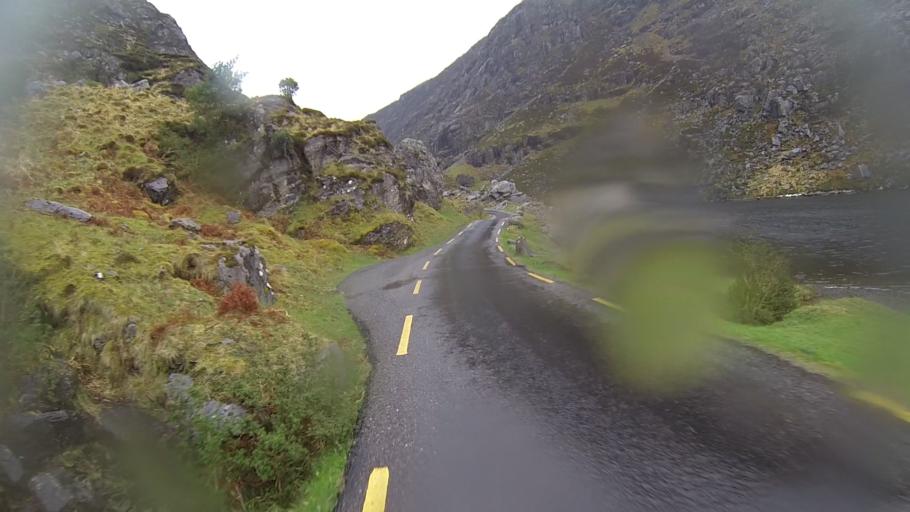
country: IE
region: Munster
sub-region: Ciarrai
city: Cill Airne
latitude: 52.0108
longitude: -9.6381
